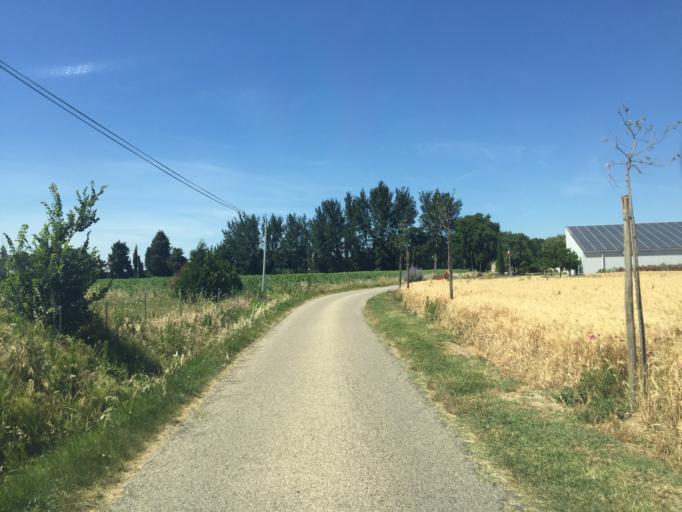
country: FR
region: Provence-Alpes-Cote d'Azur
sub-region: Departement du Vaucluse
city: Bedarrides
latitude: 44.0704
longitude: 4.9157
